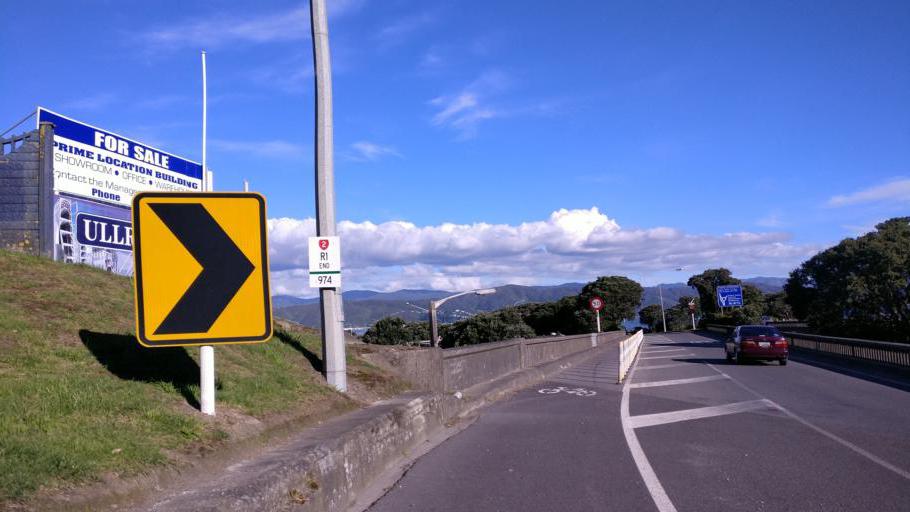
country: NZ
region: Wellington
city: Petone
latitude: -41.2235
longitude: 174.8596
